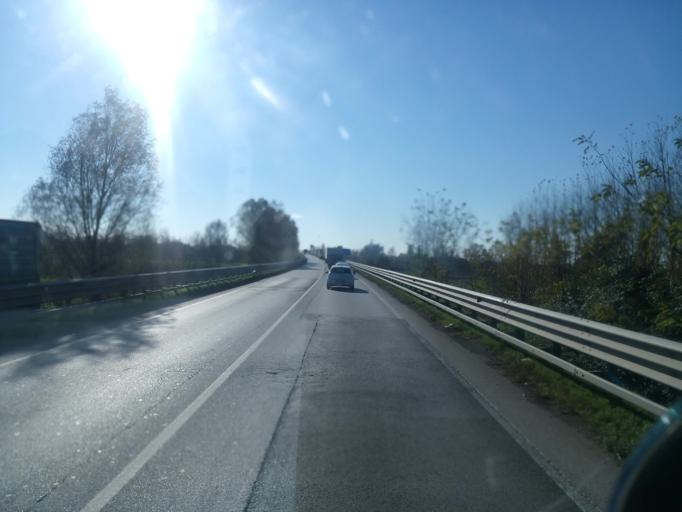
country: IT
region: Veneto
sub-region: Provincia di Padova
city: Borgoricco-San Michele delle Badesse-Sant'Eufemia
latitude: 45.5456
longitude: 11.9471
